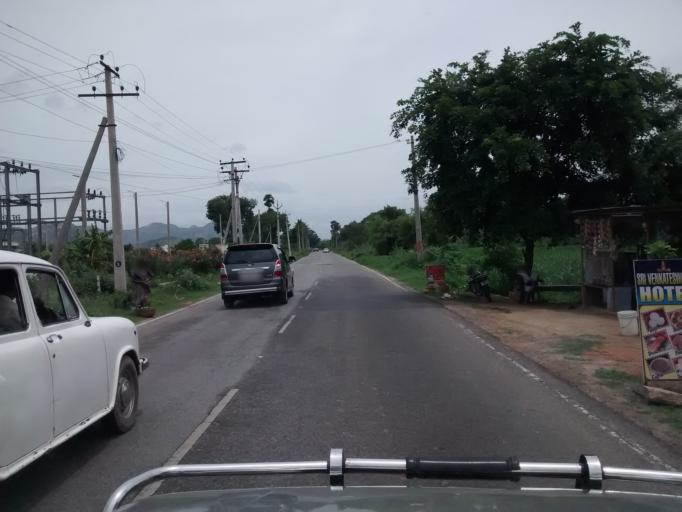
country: IN
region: Andhra Pradesh
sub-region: Chittoor
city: Narasingapuram
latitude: 13.6101
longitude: 79.3473
